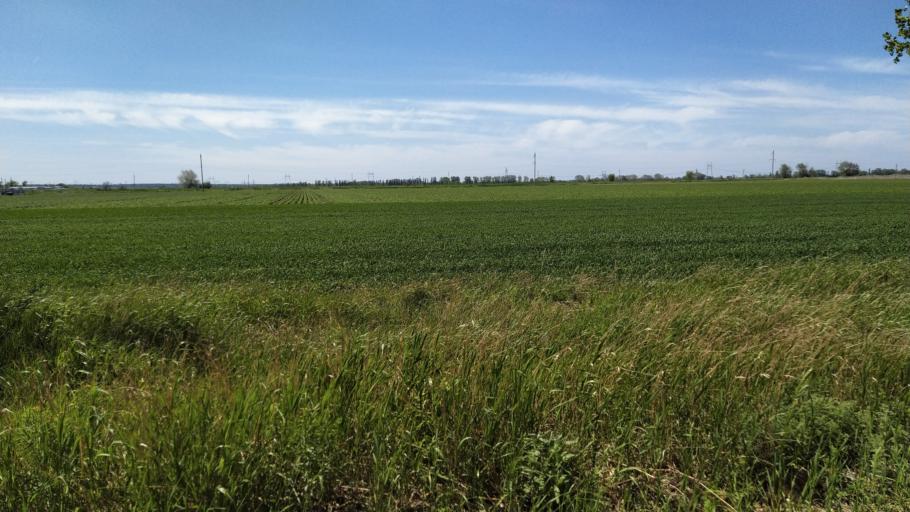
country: RU
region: Rostov
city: Kuleshovka
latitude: 47.0585
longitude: 39.6250
